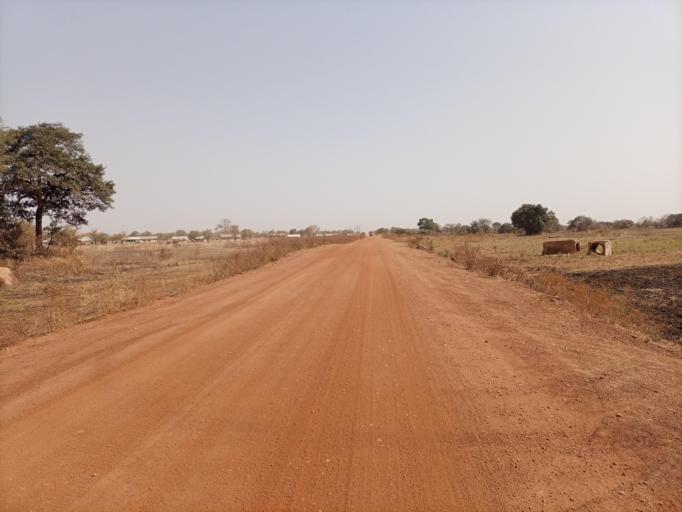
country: GH
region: Northern
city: Savelugu
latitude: 9.8129
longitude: -0.7743
